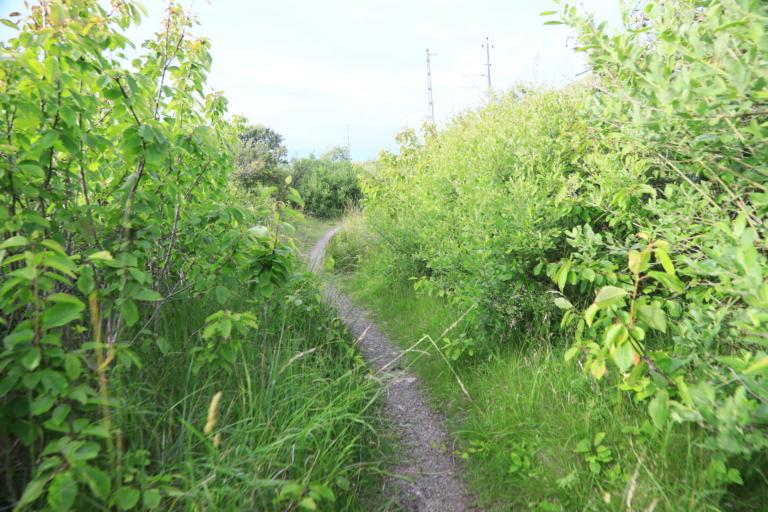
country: SE
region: Halland
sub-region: Varbergs Kommun
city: Varberg
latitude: 57.0969
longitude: 12.2443
